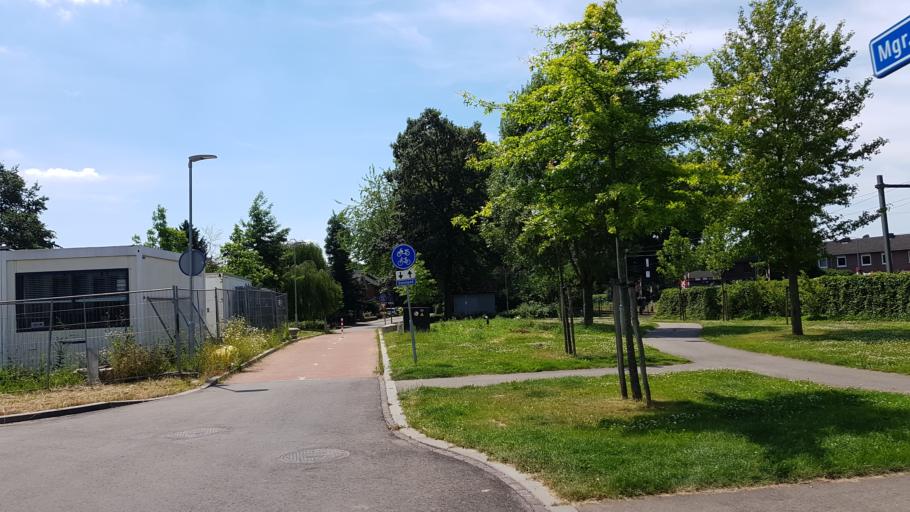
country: NL
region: Limburg
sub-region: Gemeente Sittard-Geleen
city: Sittard
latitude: 50.9934
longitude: 5.8527
